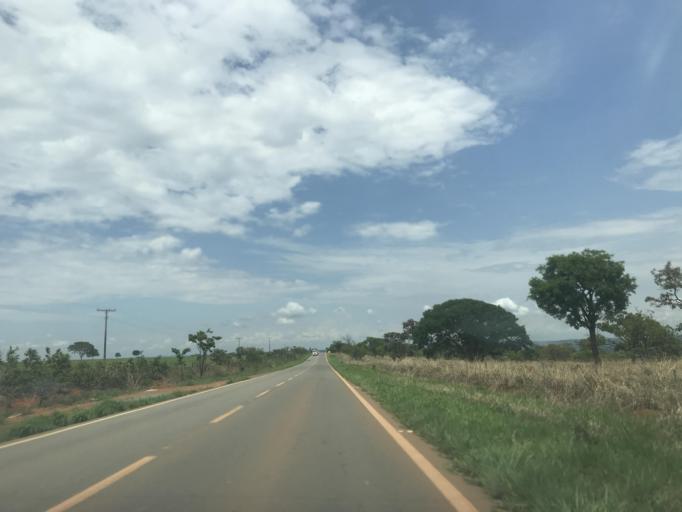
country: BR
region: Goias
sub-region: Luziania
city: Luziania
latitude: -16.3485
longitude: -48.0310
